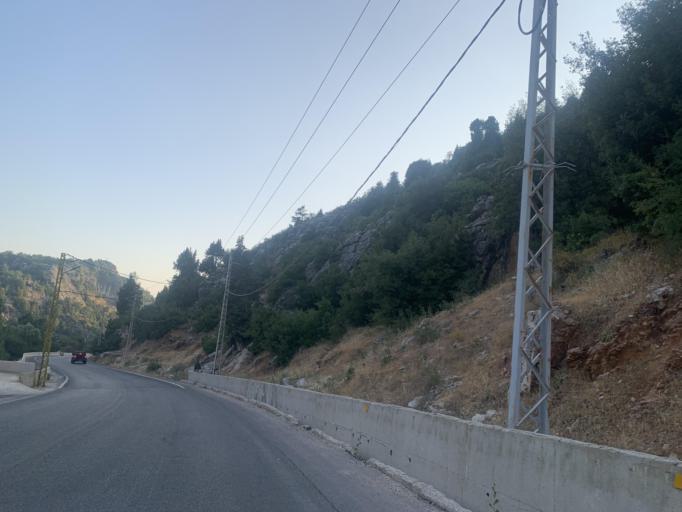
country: LB
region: Mont-Liban
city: Jbail
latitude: 34.1317
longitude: 35.8134
